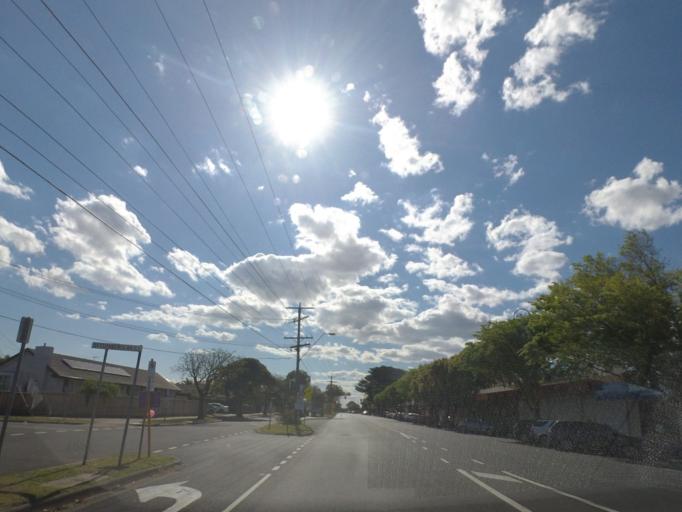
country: AU
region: Victoria
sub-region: Kingston
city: Dingley Village
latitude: -37.9841
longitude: 145.1334
